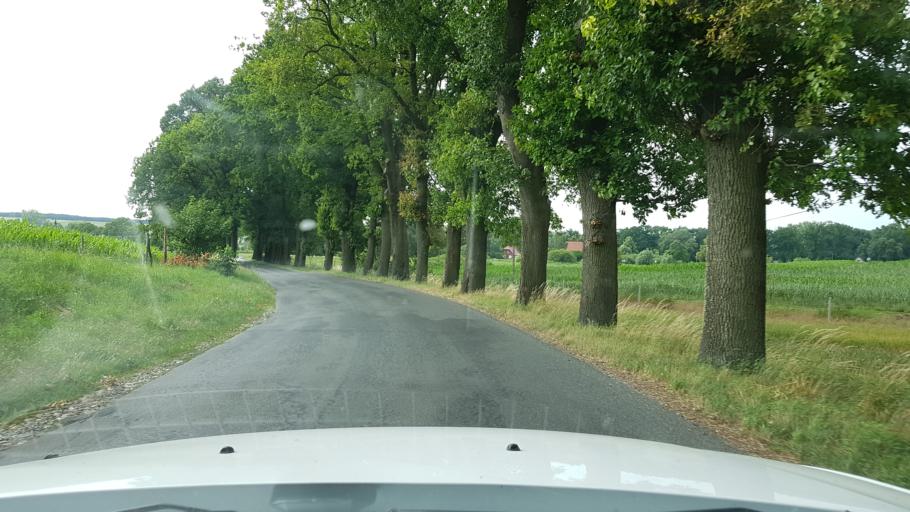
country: PL
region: West Pomeranian Voivodeship
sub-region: Powiat gryfinski
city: Moryn
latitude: 52.9150
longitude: 14.3657
